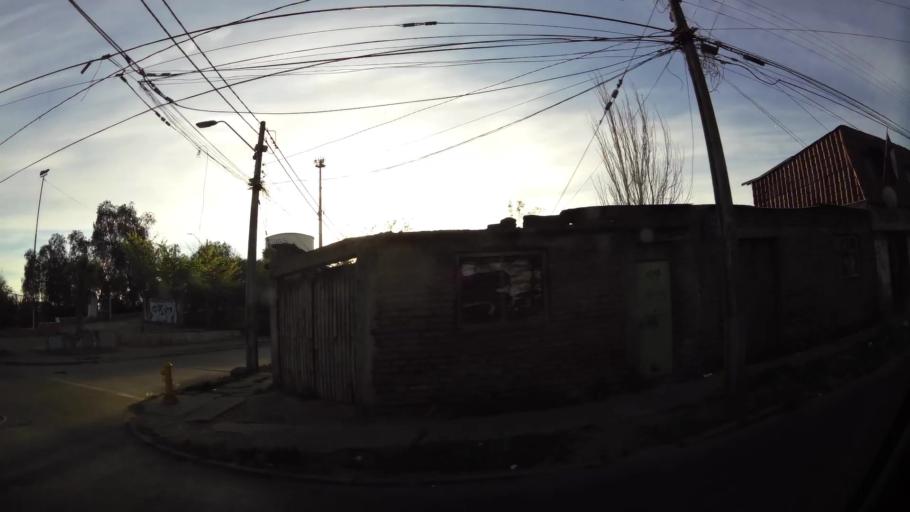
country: CL
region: Santiago Metropolitan
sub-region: Provincia de Santiago
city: Lo Prado
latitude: -33.4239
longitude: -70.7185
